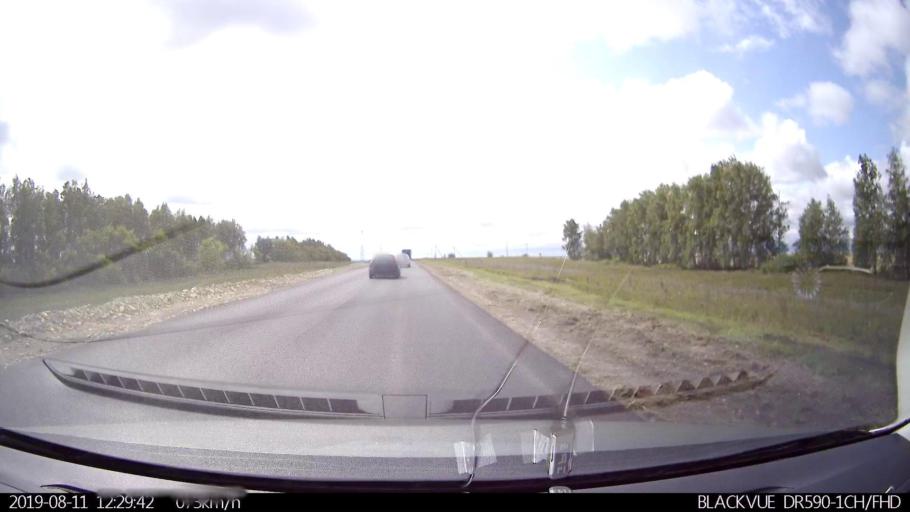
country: RU
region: Ulyanovsk
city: Ignatovka
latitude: 53.8324
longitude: 47.9002
